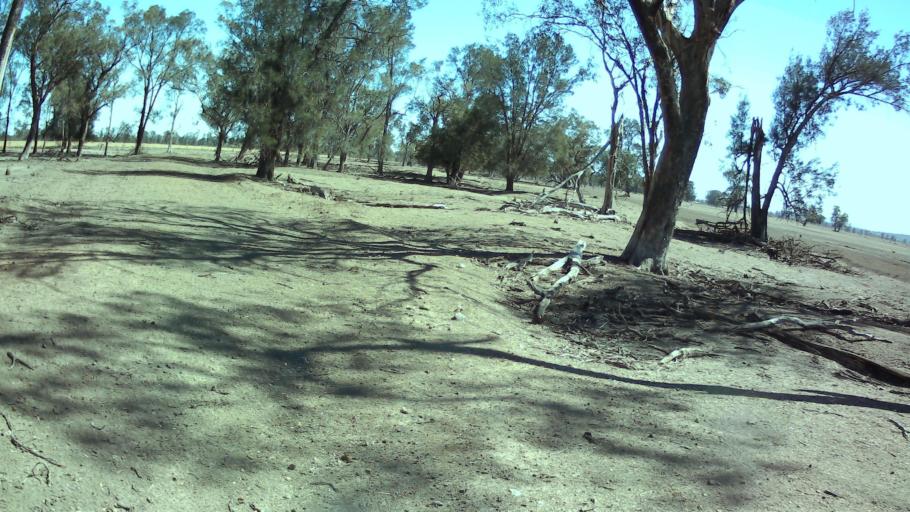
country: AU
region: New South Wales
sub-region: Bland
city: West Wyalong
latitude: -33.7693
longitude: 147.6575
